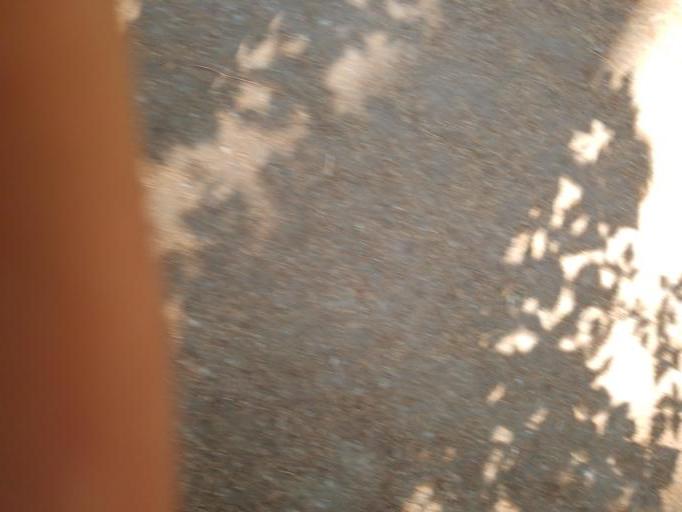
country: CA
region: British Columbia
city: West End
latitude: 49.2522
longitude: -123.2198
